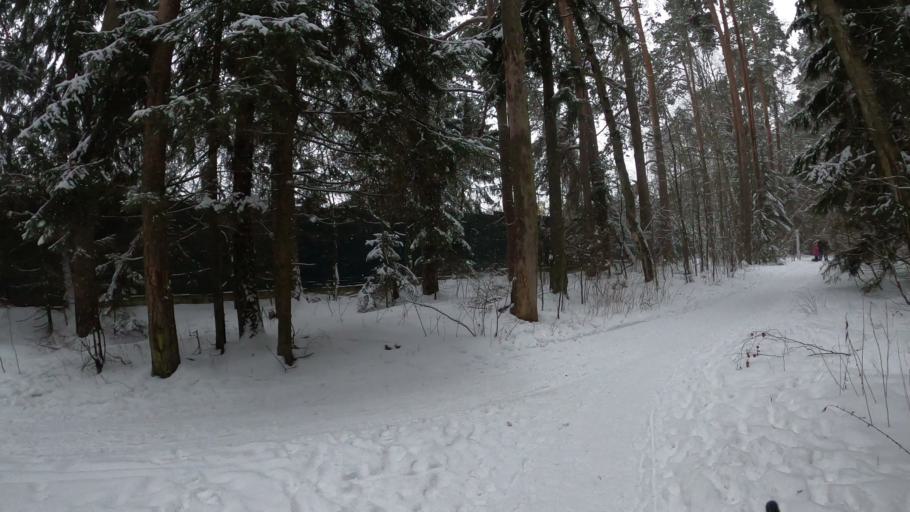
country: RU
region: Moskovskaya
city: Firsanovka
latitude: 55.9249
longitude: 37.2158
